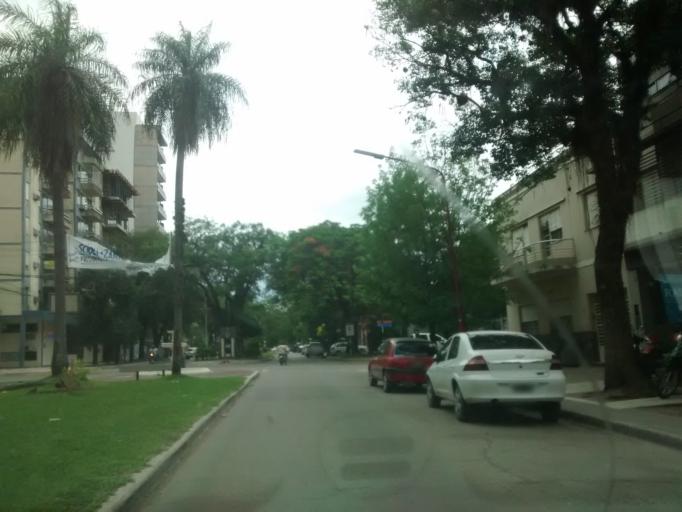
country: AR
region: Chaco
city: Resistencia
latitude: -27.4498
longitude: -58.9851
